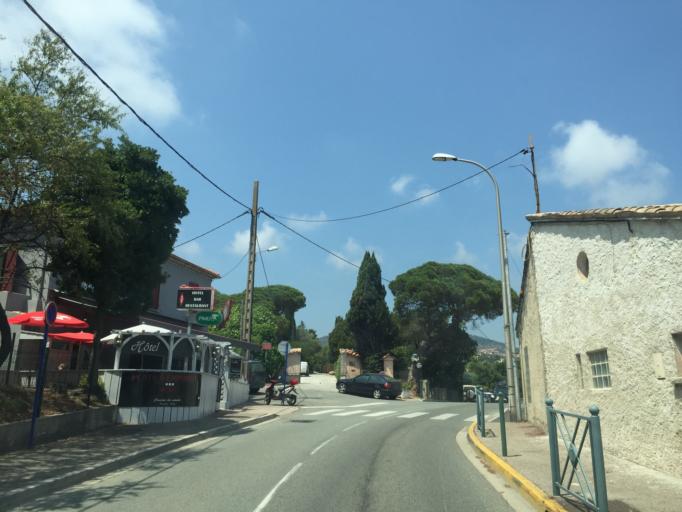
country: FR
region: Provence-Alpes-Cote d'Azur
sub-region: Departement du Var
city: Sainte-Maxime
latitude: 43.3416
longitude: 6.6799
